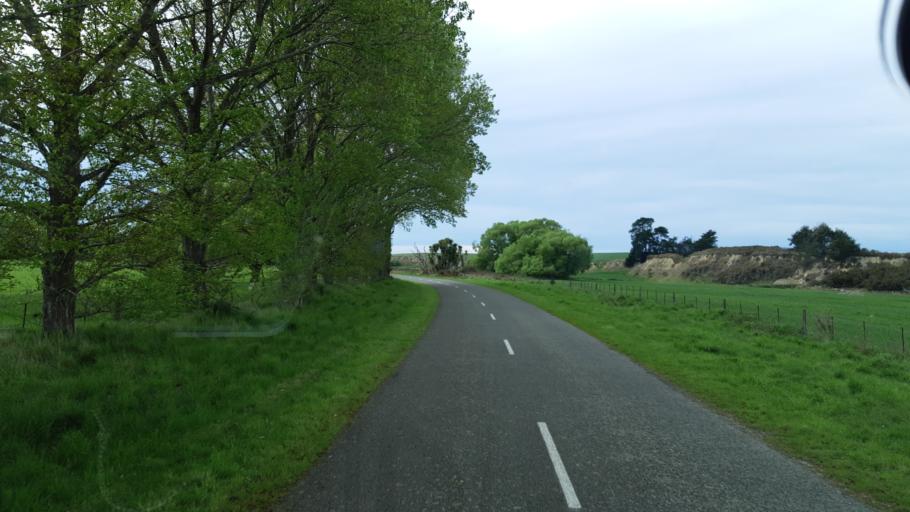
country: NZ
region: Canterbury
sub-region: Timaru District
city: Timaru
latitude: -44.5396
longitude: 171.1341
